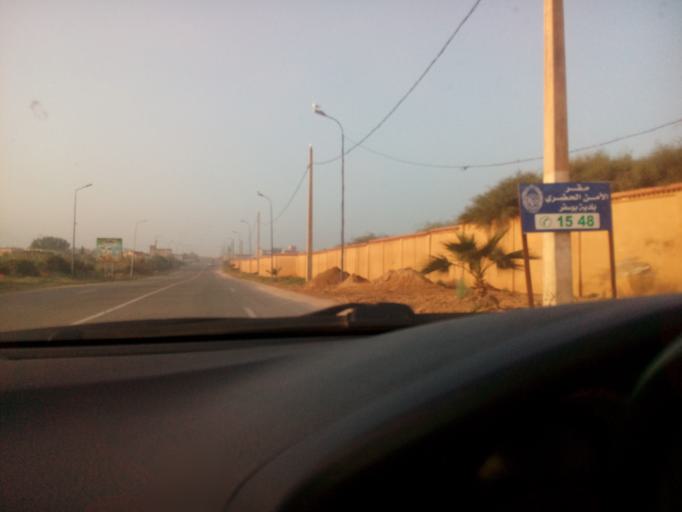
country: DZ
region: Oran
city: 'Ain el Turk
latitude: 35.7245
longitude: -0.8468
